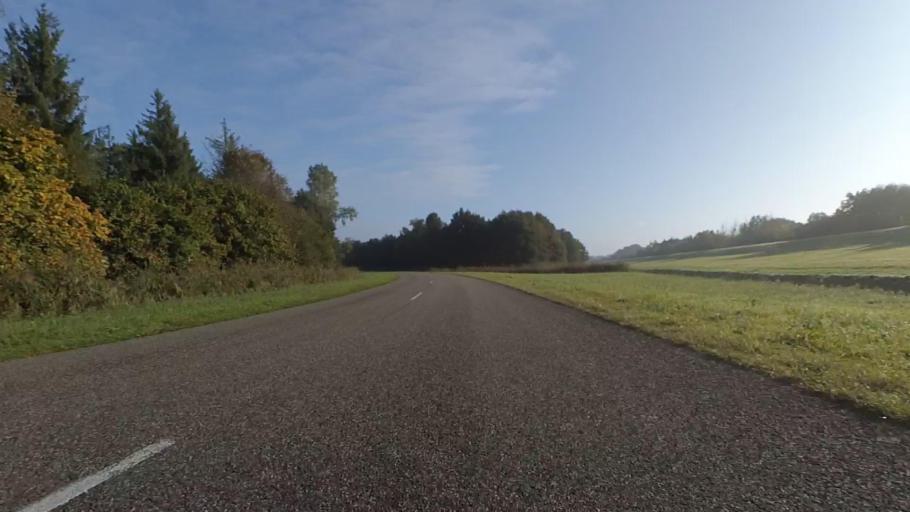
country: NL
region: Gelderland
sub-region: Gemeente Nijkerk
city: Nijkerk
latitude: 52.2725
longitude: 5.5090
